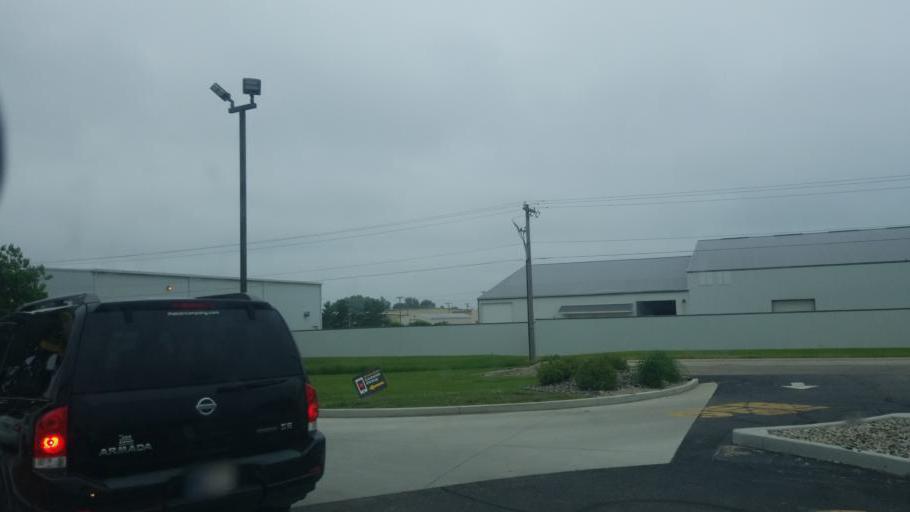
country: US
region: Indiana
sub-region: Marshall County
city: Bremen
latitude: 41.4471
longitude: -86.1670
